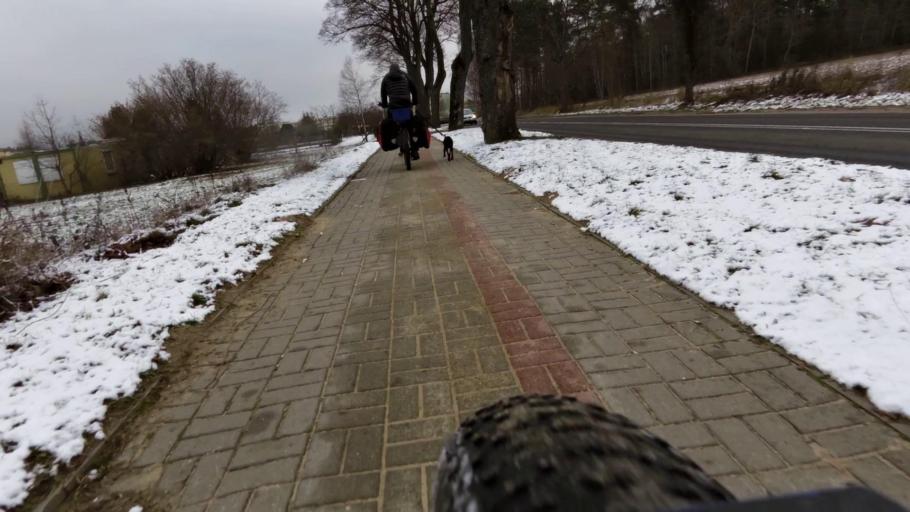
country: PL
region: West Pomeranian Voivodeship
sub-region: Powiat walecki
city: Miroslawiec
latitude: 53.3682
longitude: 16.0845
